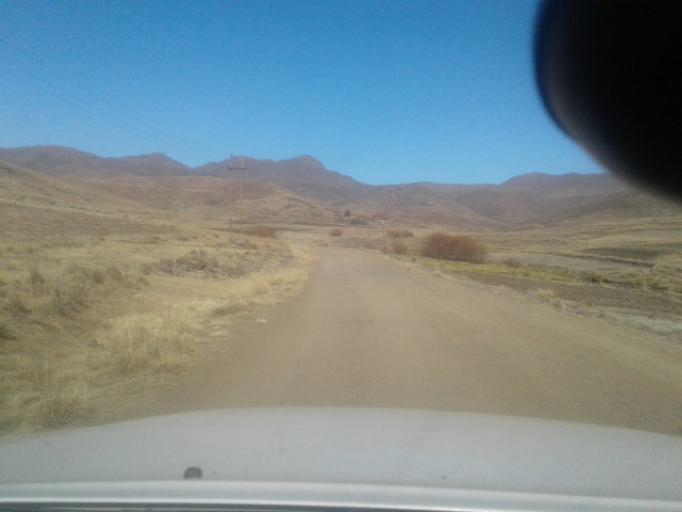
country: LS
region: Maseru
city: Nako
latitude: -29.3753
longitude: 28.0189
